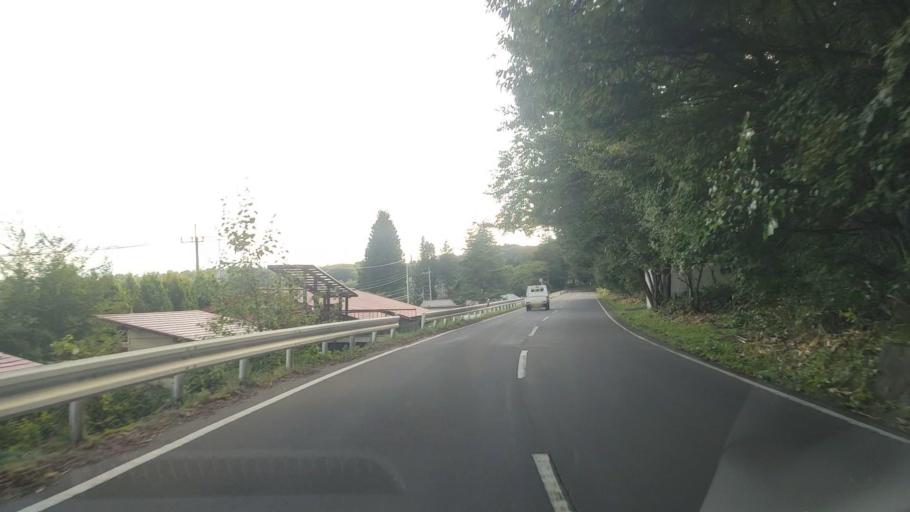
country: JP
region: Nagano
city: Nakano
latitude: 36.5854
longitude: 138.5716
